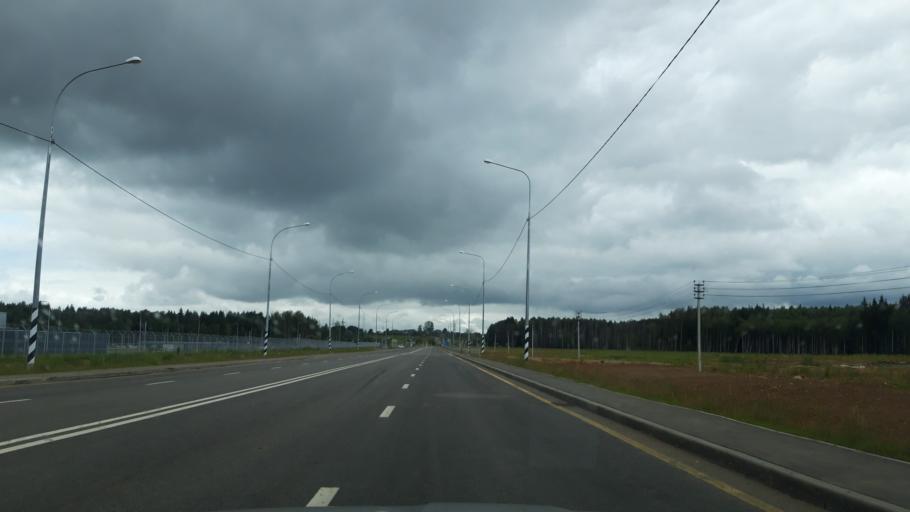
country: RU
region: Moskovskaya
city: Lozhki
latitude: 56.0842
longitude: 37.0854
